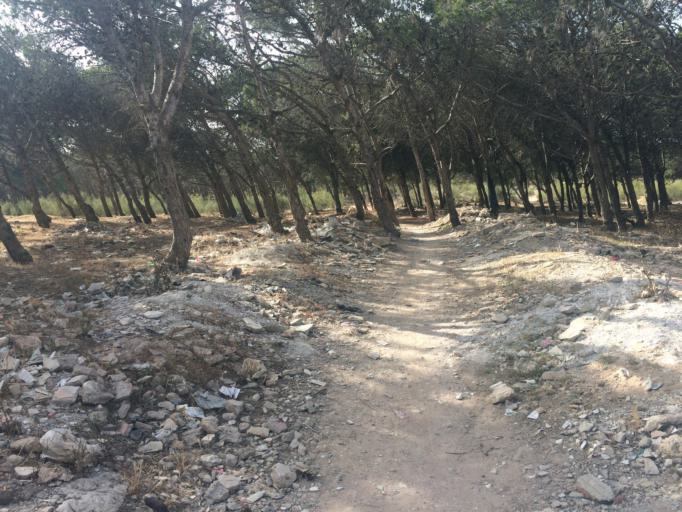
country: MA
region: Doukkala-Abda
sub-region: Safi
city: Safi
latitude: 32.3163
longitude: -9.2323
